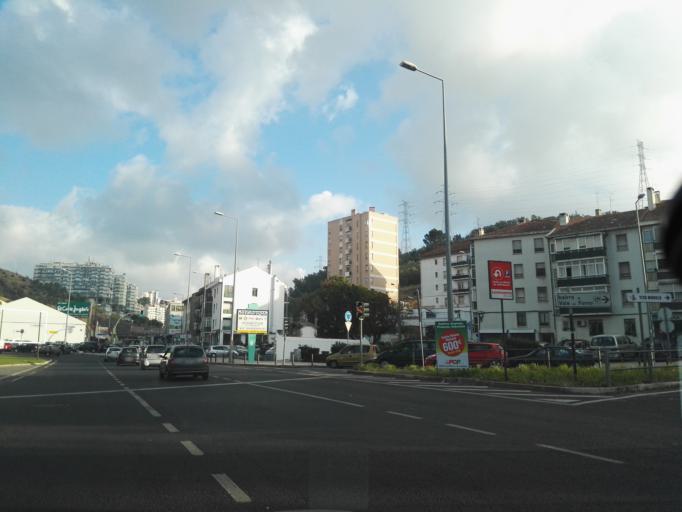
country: PT
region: Lisbon
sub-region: Odivelas
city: Olival do Basto
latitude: 38.7867
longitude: -9.1714
